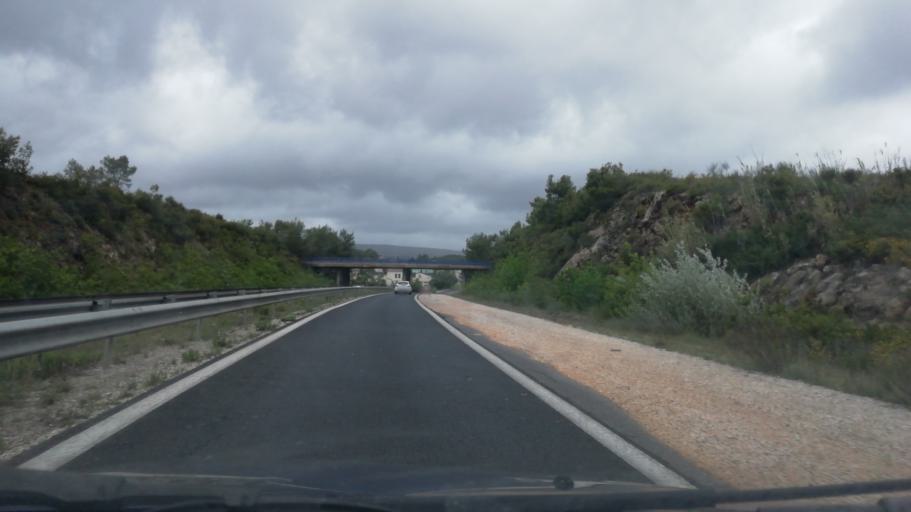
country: FR
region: Languedoc-Roussillon
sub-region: Departement de l'Herault
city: Saint-Clement-de-Riviere
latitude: 43.6728
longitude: 3.8202
